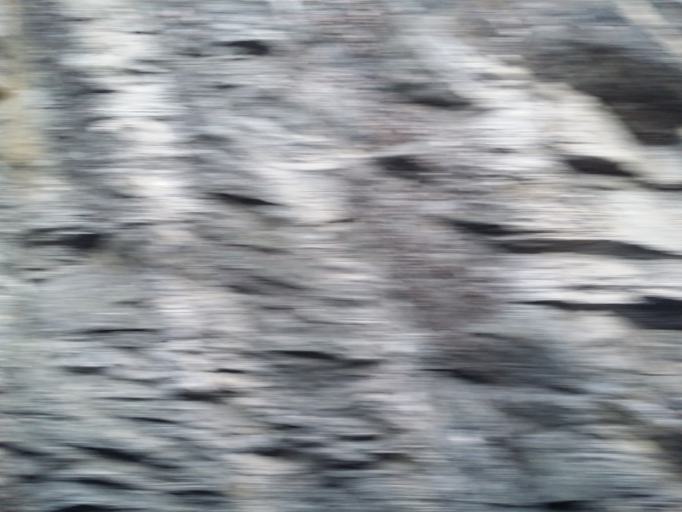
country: NO
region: Akershus
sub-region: Oppegard
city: Kolbotn
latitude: 59.8784
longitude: 10.8423
